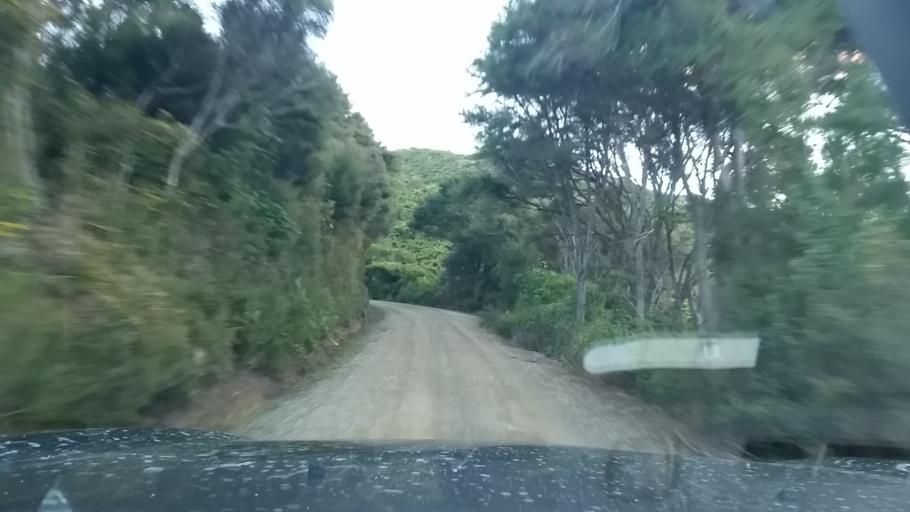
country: NZ
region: Marlborough
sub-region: Marlborough District
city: Picton
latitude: -41.1303
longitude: 174.1505
